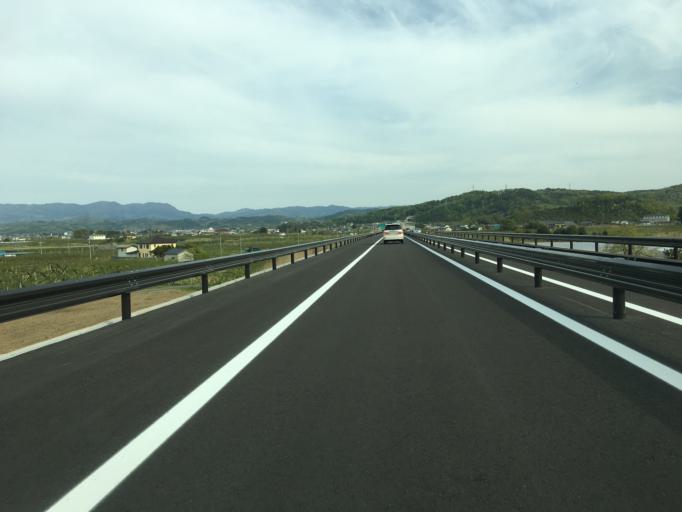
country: JP
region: Fukushima
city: Hobaramachi
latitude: 37.8196
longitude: 140.5263
